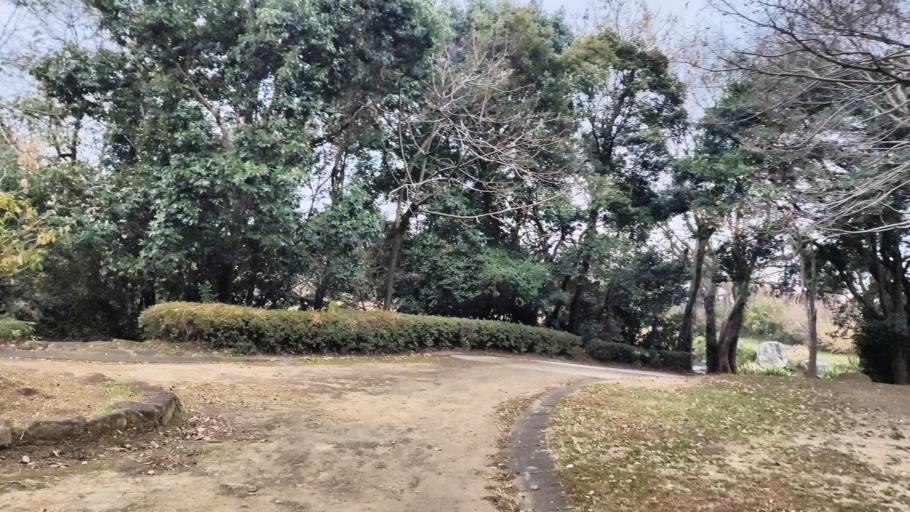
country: JP
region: Kumamoto
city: Kumamoto
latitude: 32.7842
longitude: 130.7347
